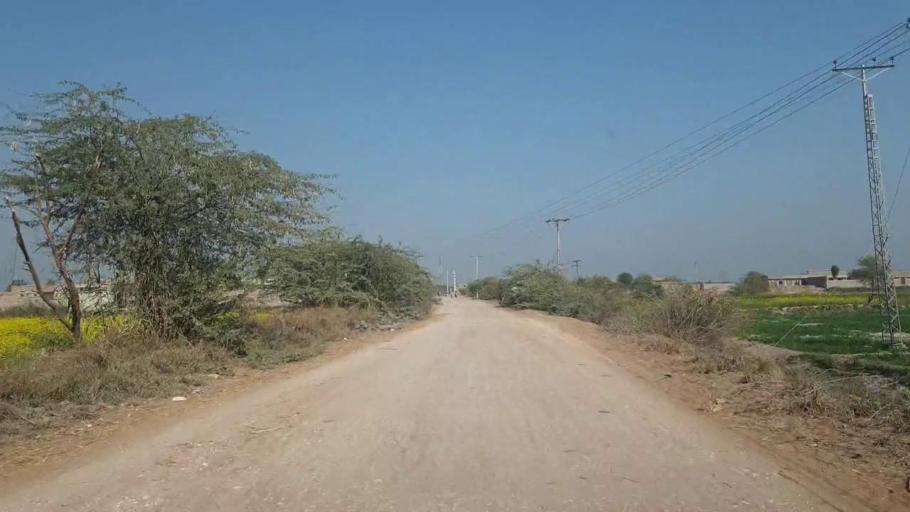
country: PK
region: Sindh
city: Sakrand
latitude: 26.0450
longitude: 68.4027
